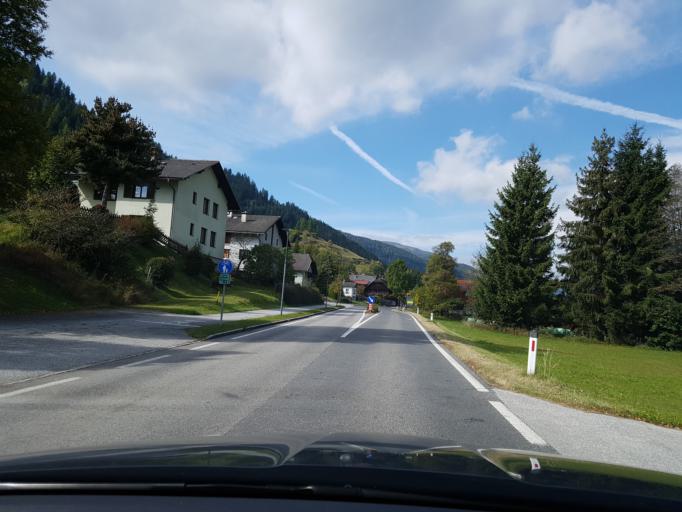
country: AT
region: Carinthia
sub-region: Politischer Bezirk Feldkirchen
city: Gnesau
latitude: 46.7763
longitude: 13.9594
